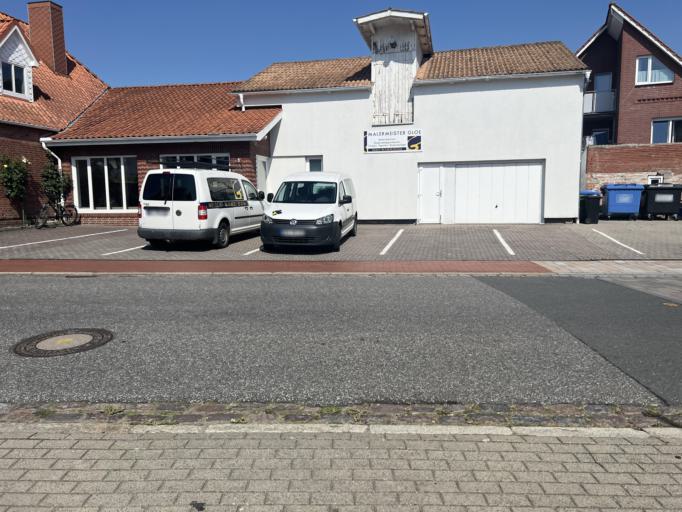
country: DE
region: Schleswig-Holstein
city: Meldorf
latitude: 54.0889
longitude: 9.0771
